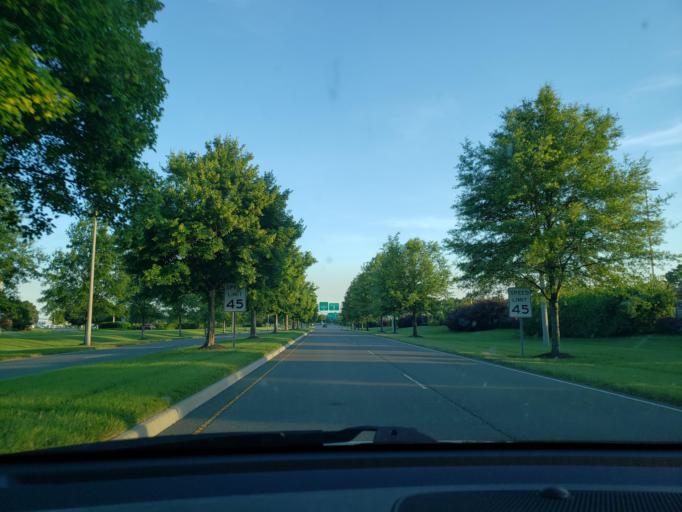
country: US
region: Virginia
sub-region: Henrico County
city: Fort Lee
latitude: 37.5092
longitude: -77.3369
